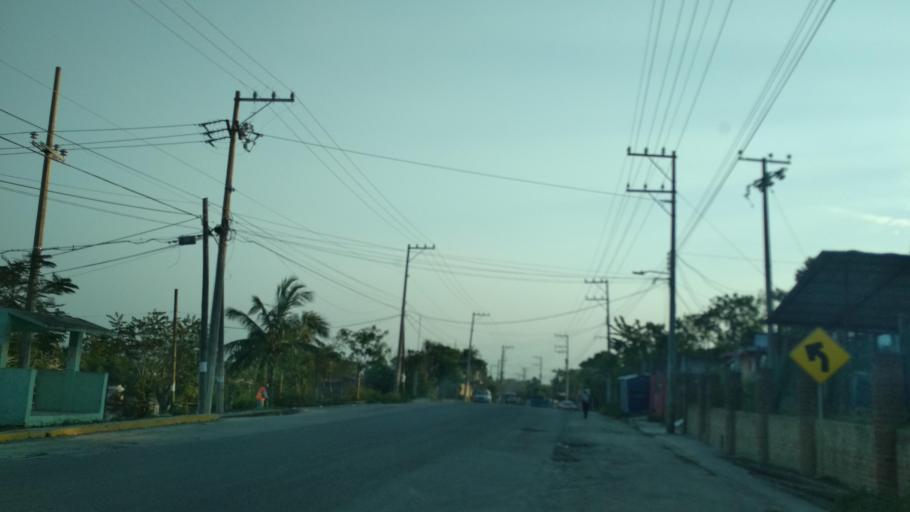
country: MM
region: Shan
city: Taunggyi
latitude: 20.4106
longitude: 97.3370
